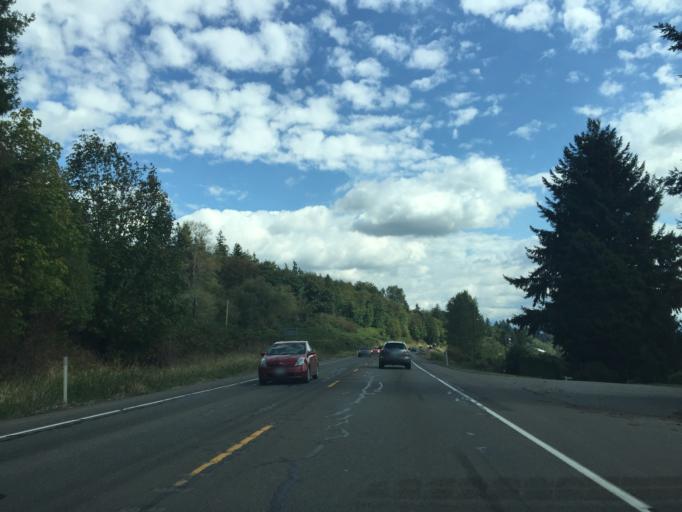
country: US
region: Washington
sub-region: Snohomish County
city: Snohomish
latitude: 47.9108
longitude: -122.0544
